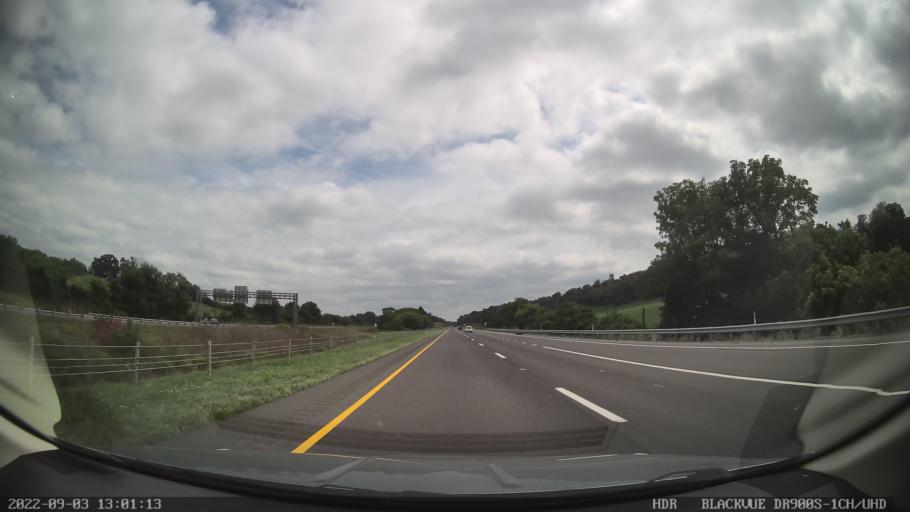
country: US
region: Pennsylvania
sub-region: Union County
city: New Columbia
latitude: 41.0480
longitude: -76.8335
